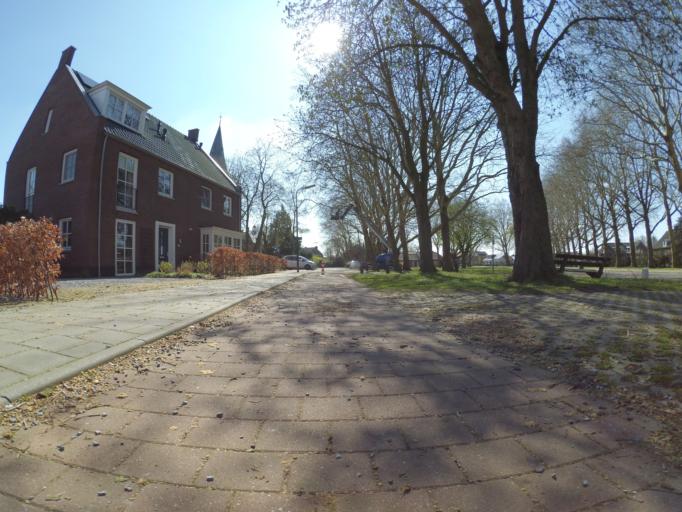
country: NL
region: Utrecht
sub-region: Gemeente Utrechtse Heuvelrug
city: Driebergen-Rijsenburg
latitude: 52.0262
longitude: 5.2444
